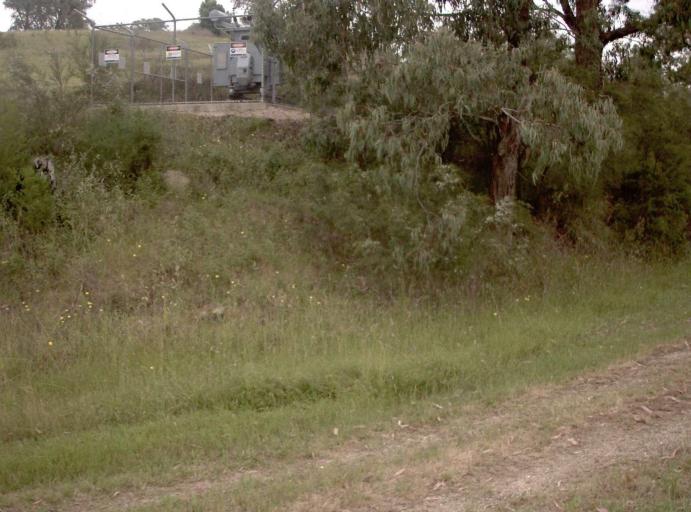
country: AU
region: Victoria
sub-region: East Gippsland
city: Bairnsdale
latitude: -37.7654
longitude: 147.3216
